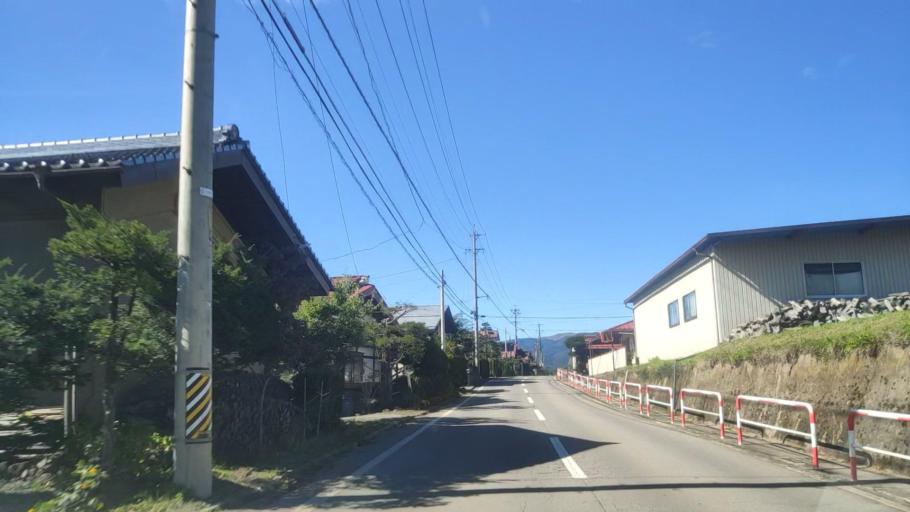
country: JP
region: Nagano
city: Chino
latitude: 36.0043
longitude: 138.2096
